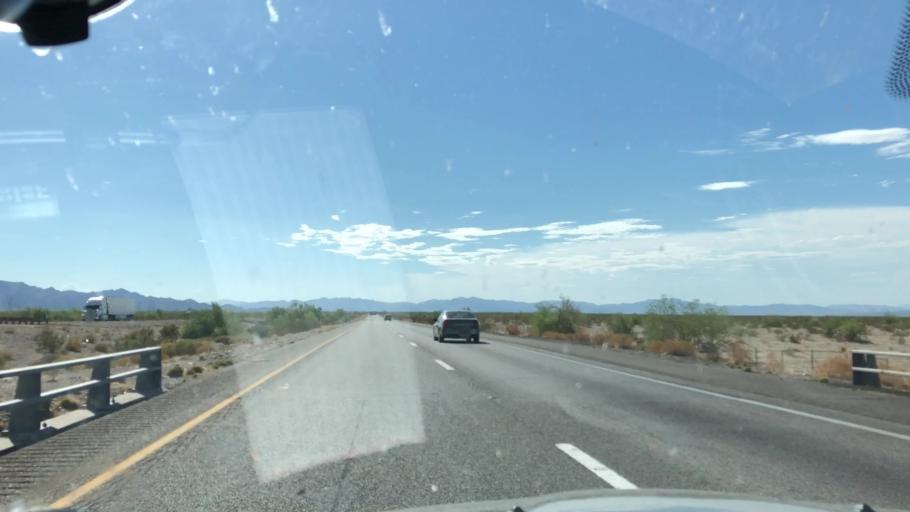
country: US
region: California
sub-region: Riverside County
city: Mesa Verde
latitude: 33.6627
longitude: -115.1762
